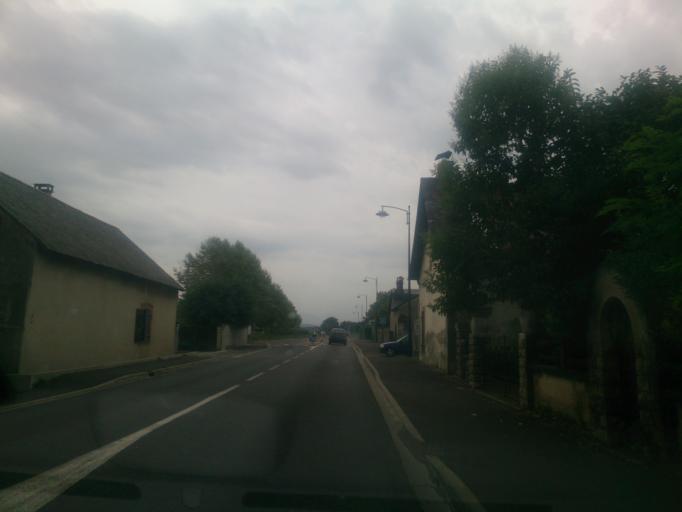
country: FR
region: Midi-Pyrenees
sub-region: Departement des Hautes-Pyrenees
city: Laloubere
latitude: 43.2016
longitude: 0.0759
